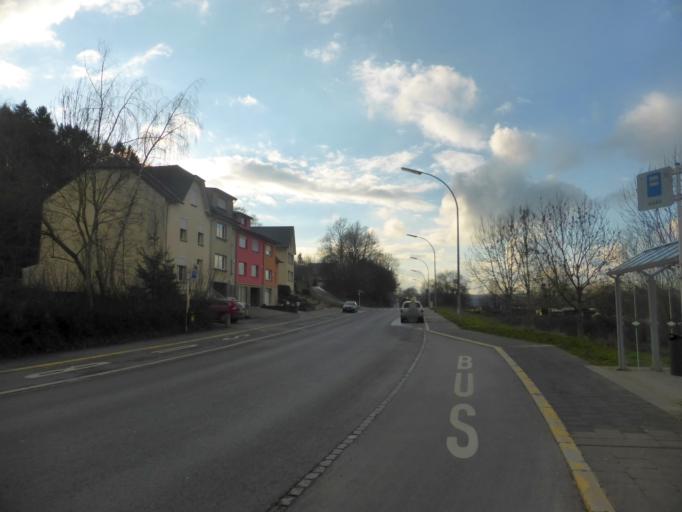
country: LU
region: Luxembourg
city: Belvaux
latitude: 49.5147
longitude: 5.9262
